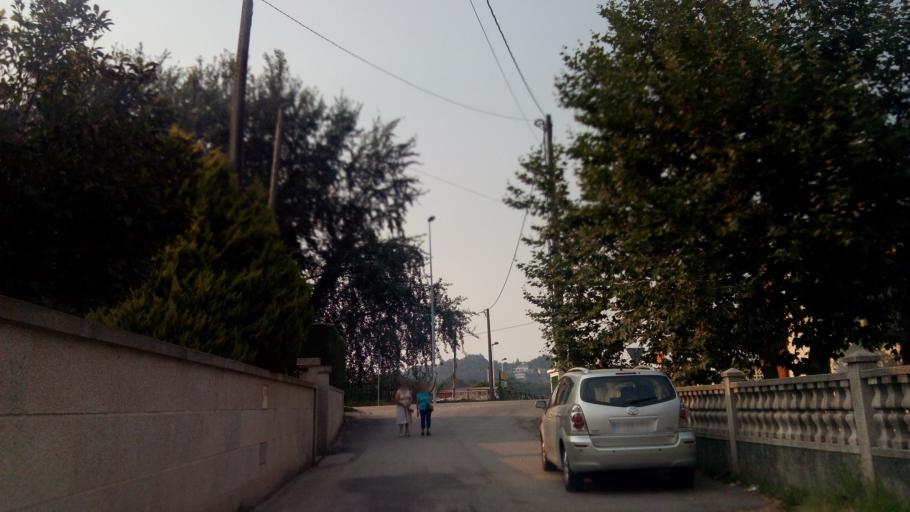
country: ES
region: Galicia
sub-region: Provincia de Pontevedra
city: Baiona
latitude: 42.1118
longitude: -8.8225
